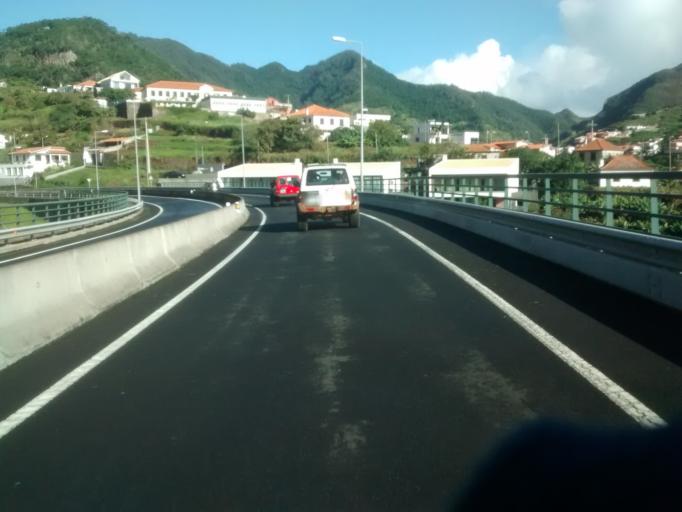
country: PT
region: Madeira
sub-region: Machico
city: Machico
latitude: 32.7286
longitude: -16.7790
